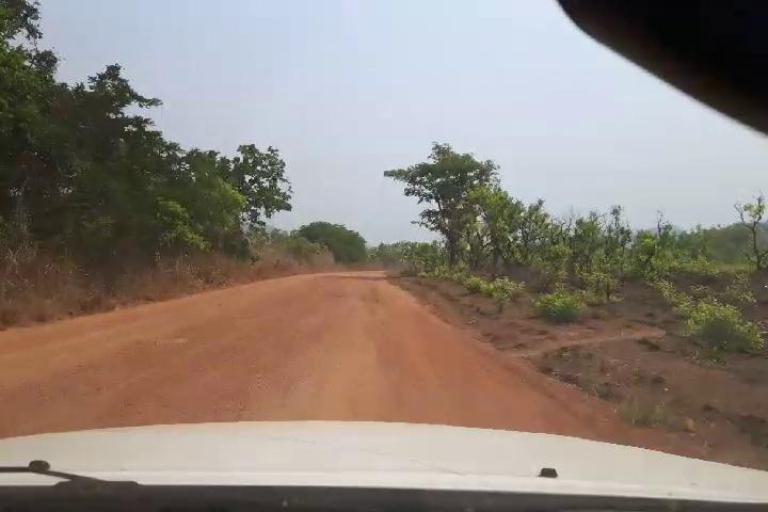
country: SL
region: Northern Province
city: Bumbuna
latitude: 8.9353
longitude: -11.8172
